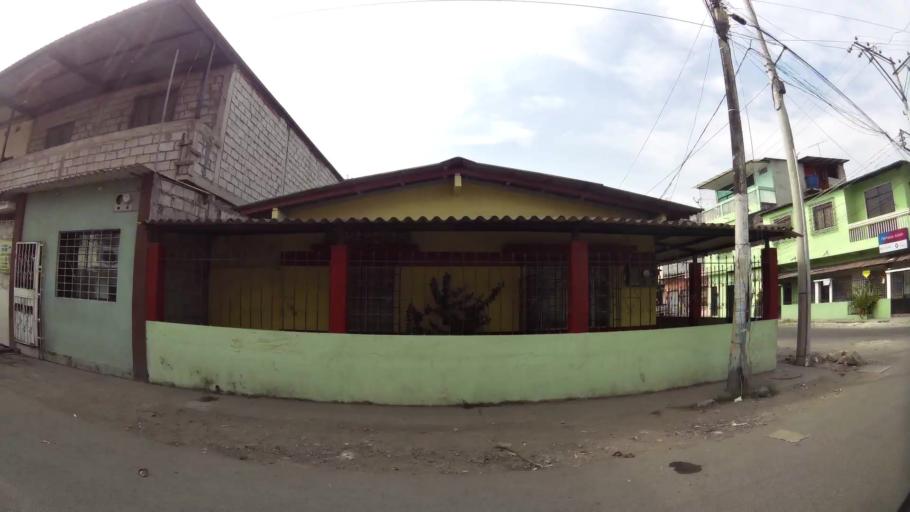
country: EC
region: Guayas
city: Guayaquil
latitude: -2.2574
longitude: -79.9052
